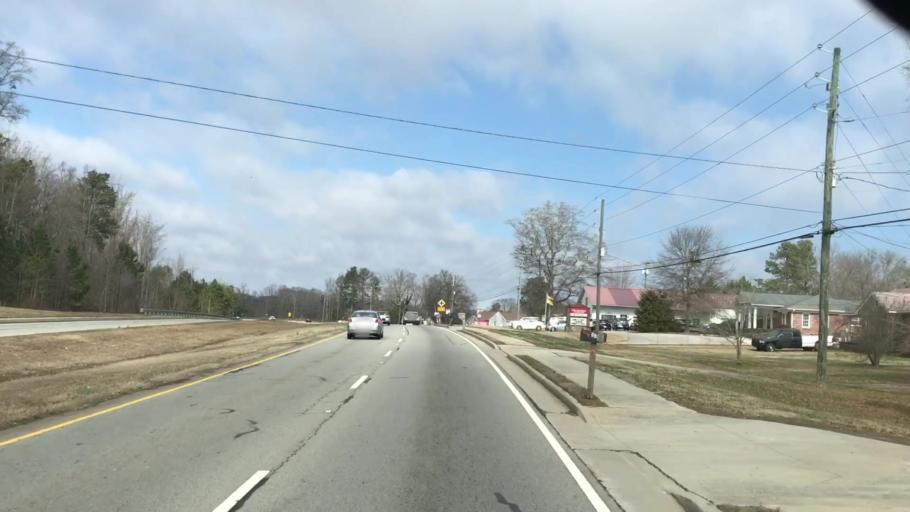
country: US
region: Georgia
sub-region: Hall County
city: Oakwood
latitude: 34.2042
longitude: -83.8562
